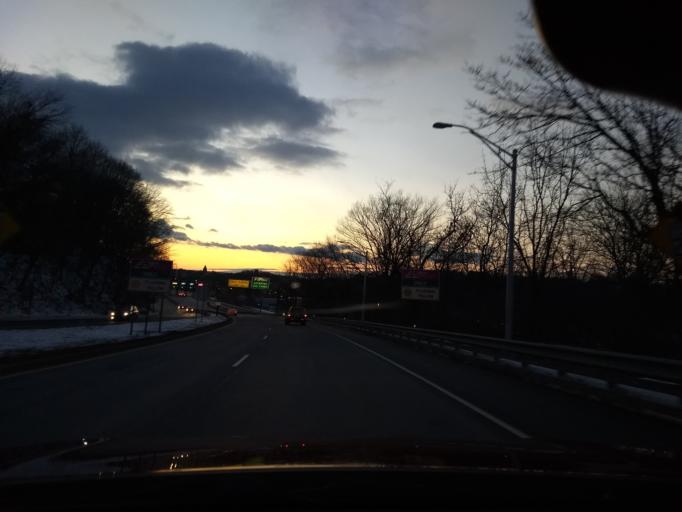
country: US
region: New Jersey
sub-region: Warren County
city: Phillipsburg
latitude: 40.6967
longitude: -75.1959
